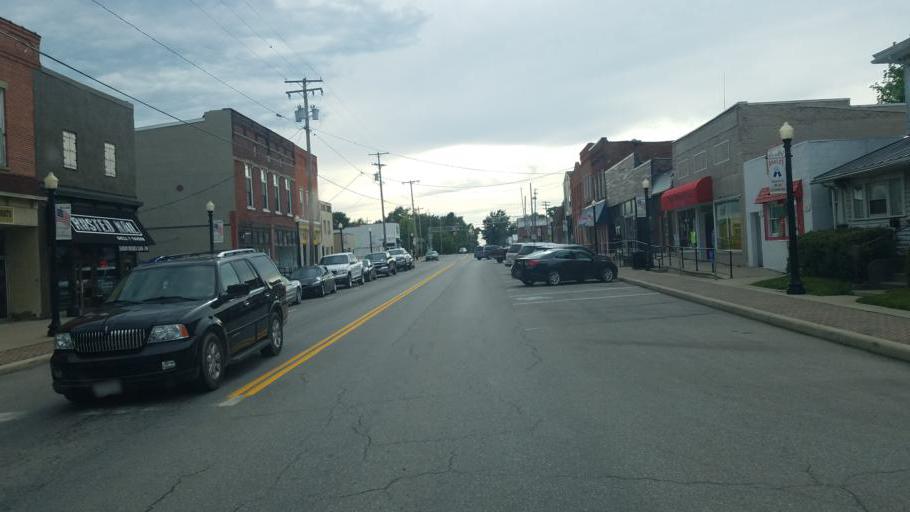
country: US
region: Ohio
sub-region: Delaware County
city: Ashley
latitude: 40.4091
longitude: -82.9536
